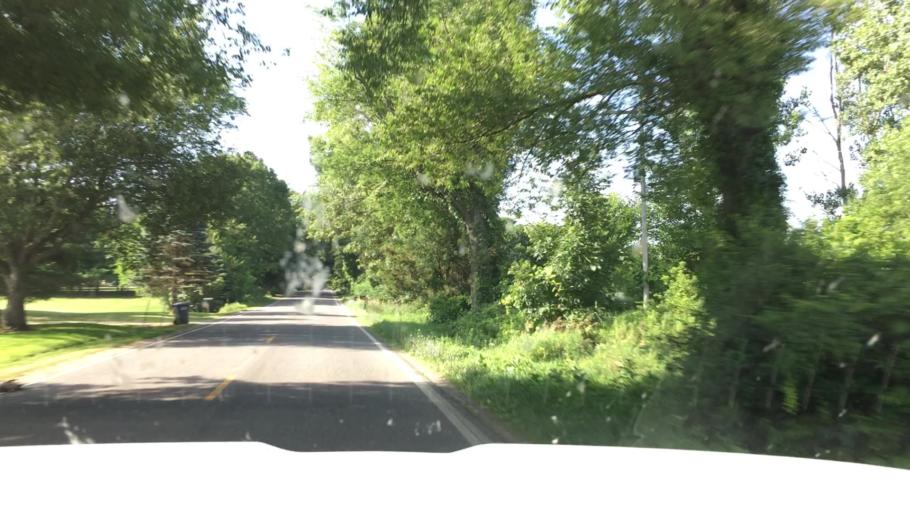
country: US
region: Michigan
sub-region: Barry County
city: Stony Point
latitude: 42.4372
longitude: -85.4545
